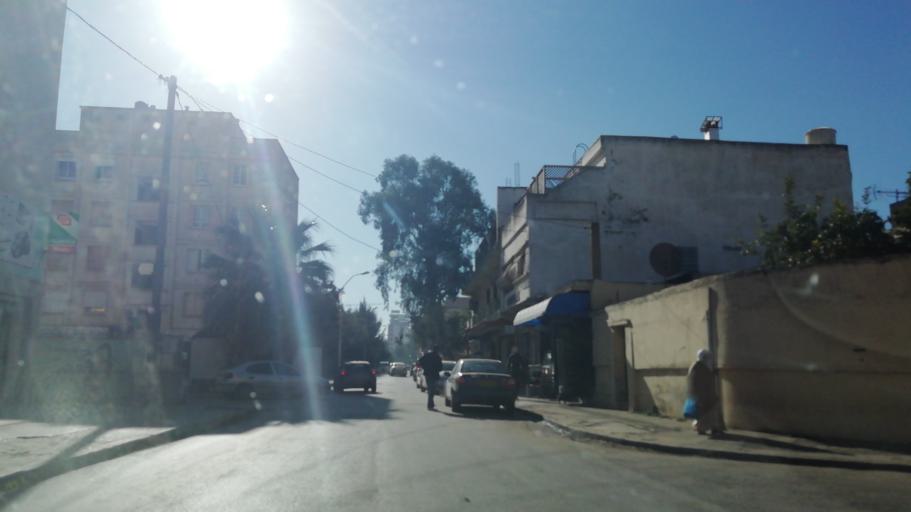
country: DZ
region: Oran
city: Oran
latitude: 35.6709
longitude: -0.6506
